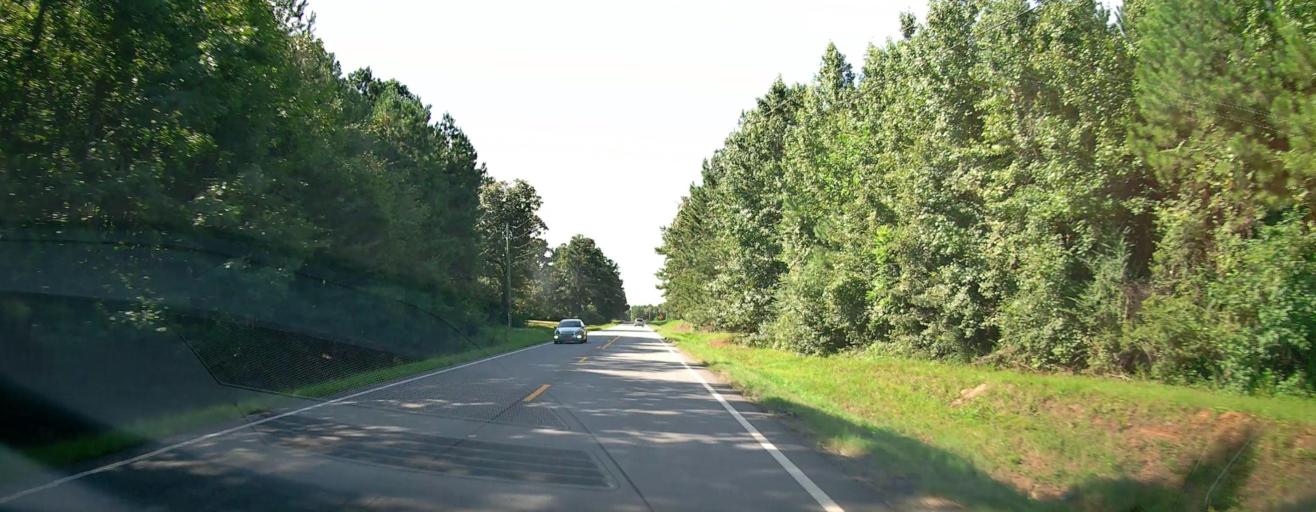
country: US
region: Georgia
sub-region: Upson County
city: Hannahs Mill
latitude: 32.9570
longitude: -84.4620
